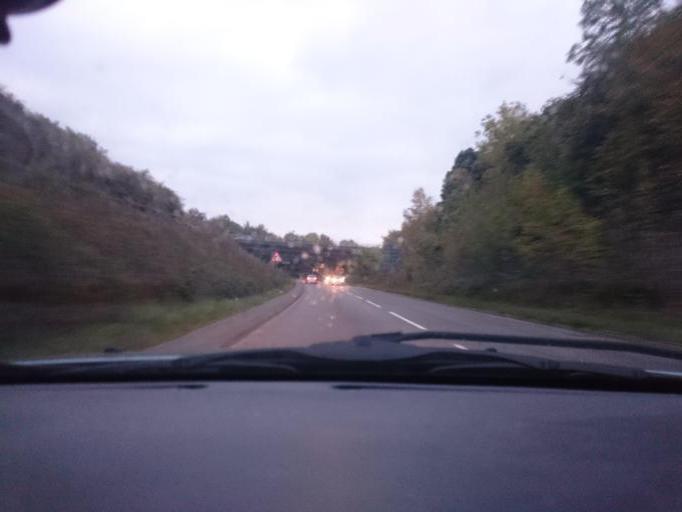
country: GB
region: England
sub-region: Surrey
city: Seale
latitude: 51.2258
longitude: -0.7330
